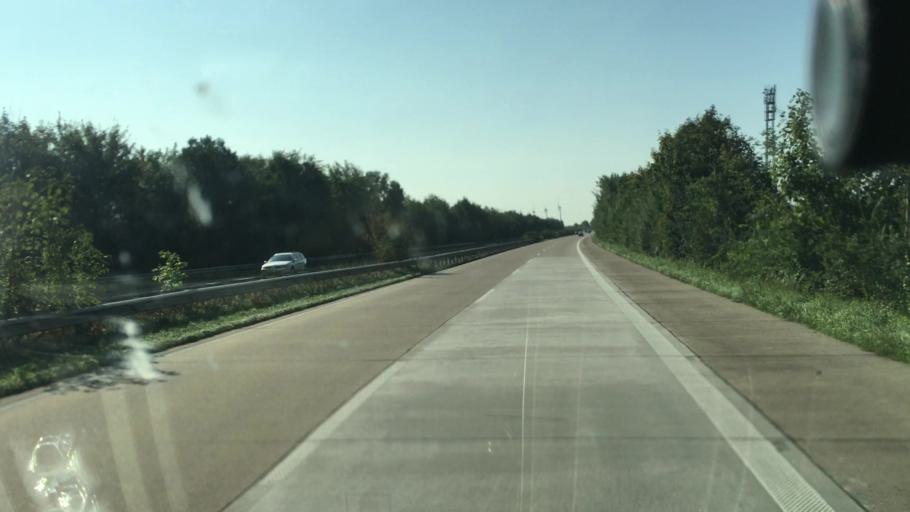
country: DE
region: Lower Saxony
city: Sande
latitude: 53.4689
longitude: 8.0166
